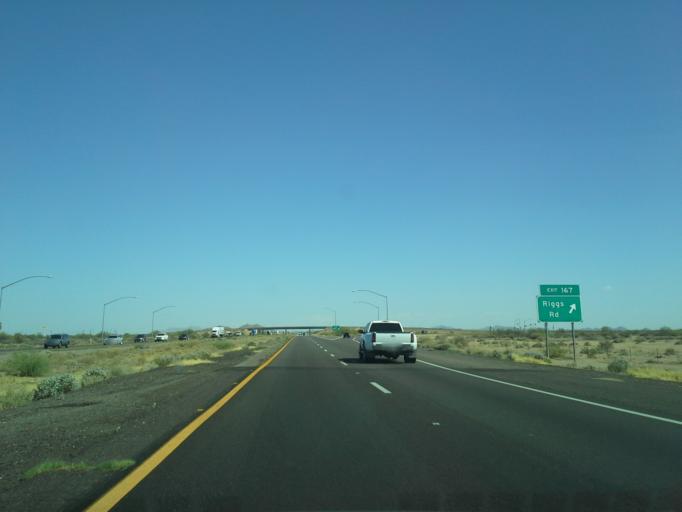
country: US
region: Arizona
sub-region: Maricopa County
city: Sun Lakes
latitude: 33.2244
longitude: -111.9244
